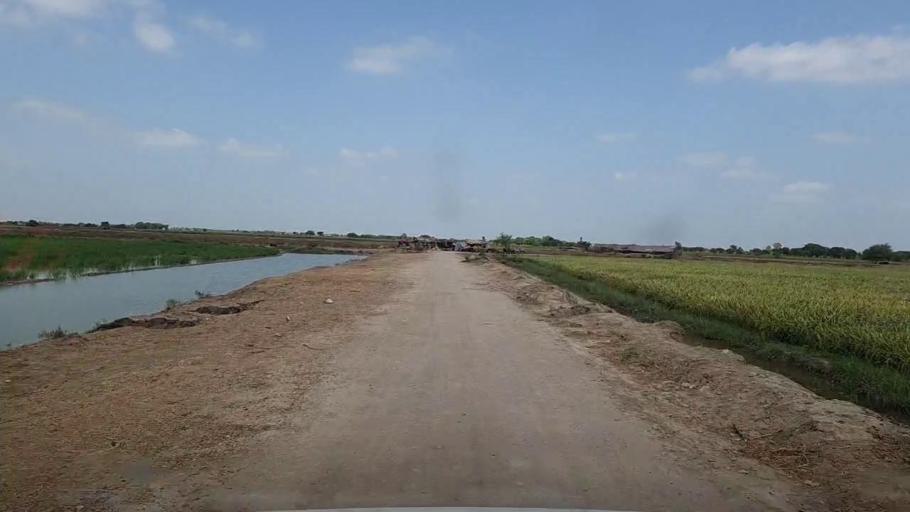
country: PK
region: Sindh
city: Kario
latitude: 24.6803
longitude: 68.5879
